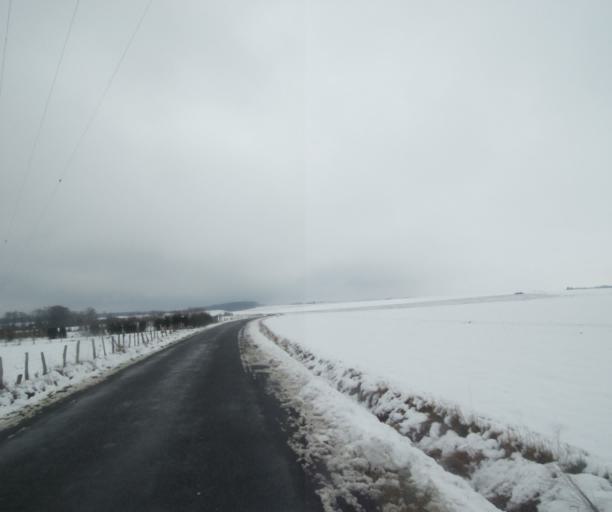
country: FR
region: Champagne-Ardenne
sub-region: Departement de la Haute-Marne
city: Montier-en-Der
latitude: 48.4716
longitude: 4.7925
